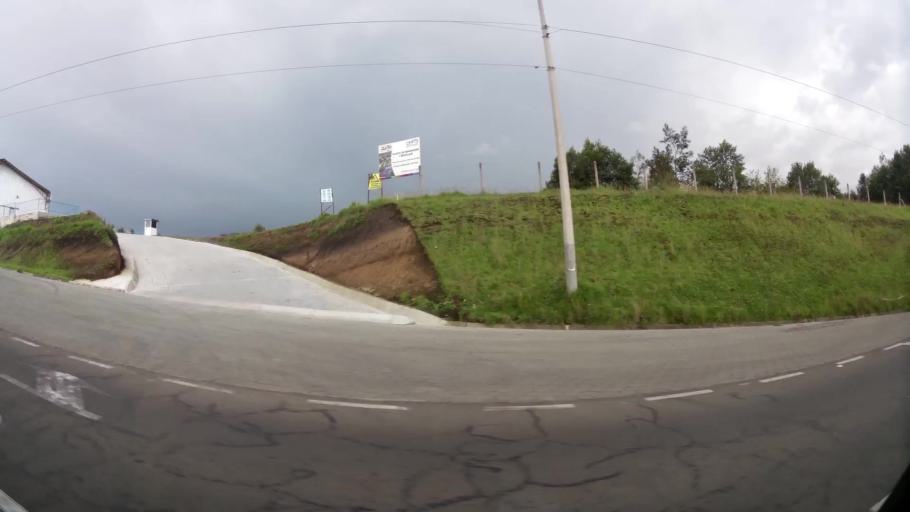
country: EC
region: Pichincha
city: Sangolqui
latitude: -0.3102
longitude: -78.5220
